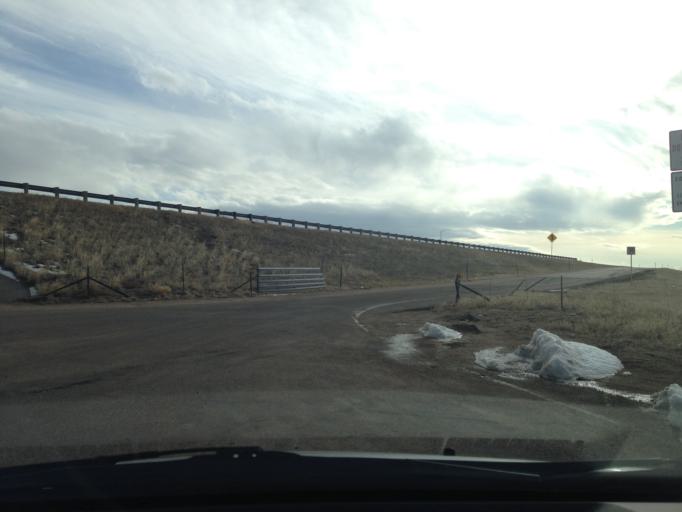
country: US
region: Colorado
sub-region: Weld County
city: Keenesburg
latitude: 40.2164
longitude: -104.2153
